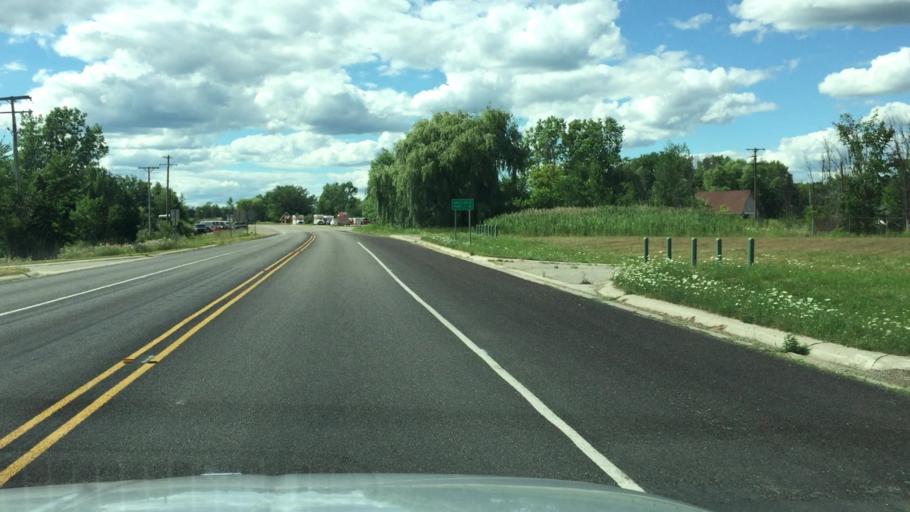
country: US
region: Michigan
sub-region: Saint Clair County
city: Capac
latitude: 43.0228
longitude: -82.9290
